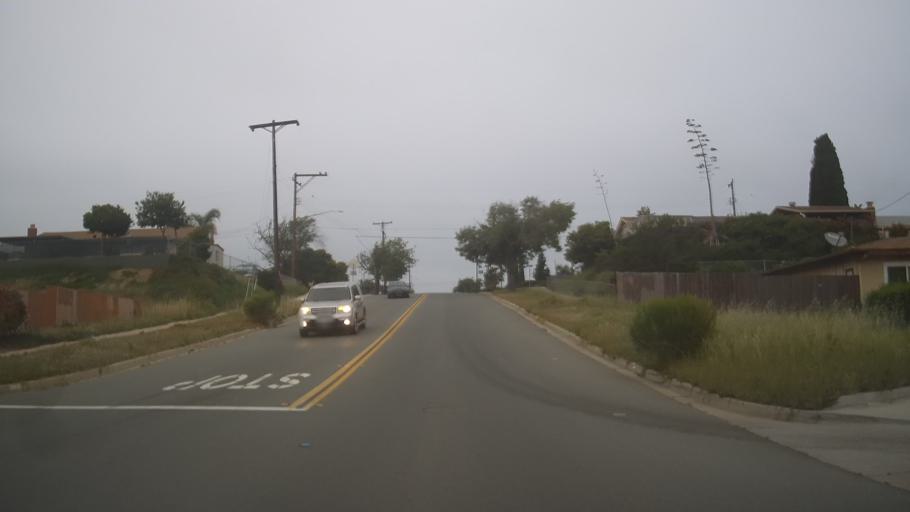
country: US
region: California
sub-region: San Diego County
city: Bonita
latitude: 32.6231
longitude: -117.0479
